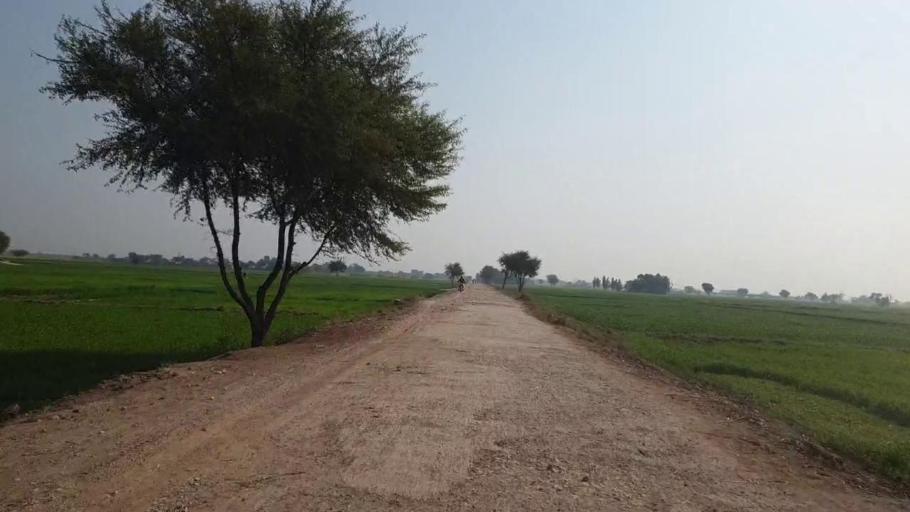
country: PK
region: Sindh
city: Bhit Shah
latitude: 25.7346
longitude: 68.5262
